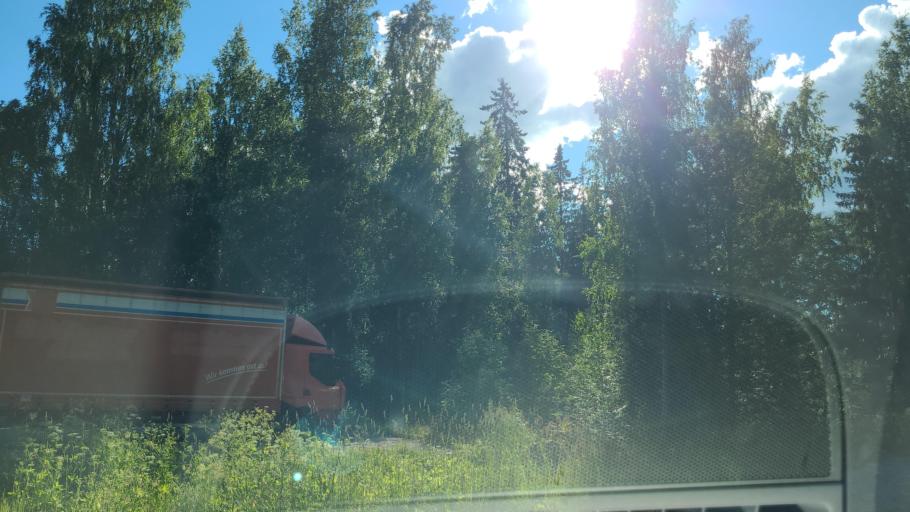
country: FI
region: Pirkanmaa
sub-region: Tampere
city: Kangasala
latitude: 61.5443
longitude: 24.0412
